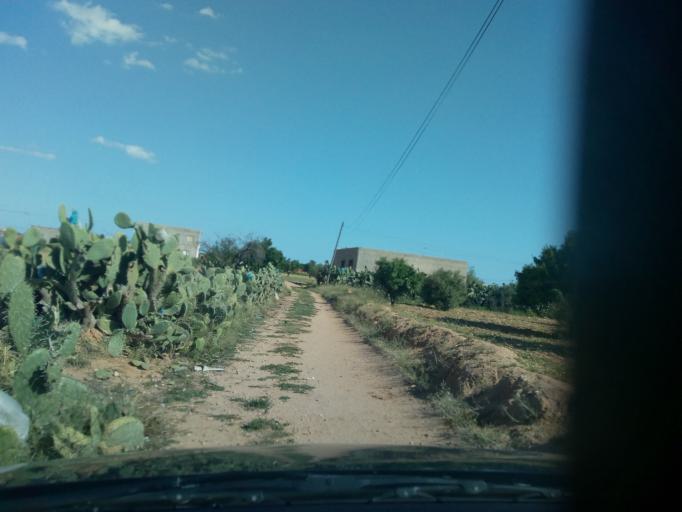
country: TN
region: Safaqis
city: Sfax
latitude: 34.7270
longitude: 10.6014
